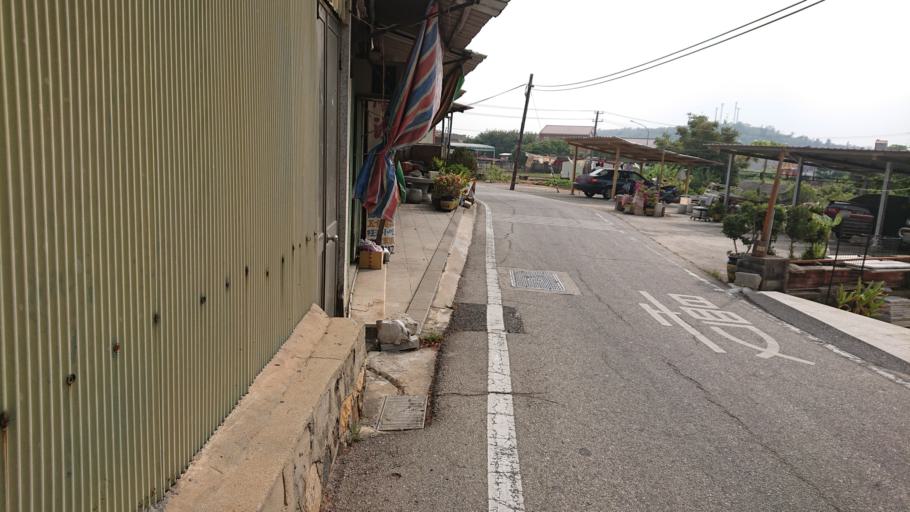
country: TW
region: Fukien
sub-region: Kinmen
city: Jincheng
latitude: 24.4317
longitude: 118.2475
